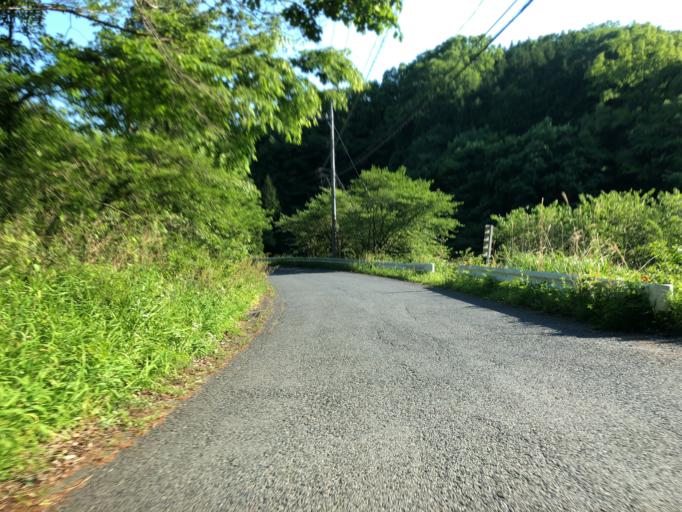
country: JP
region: Ibaraki
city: Kitaibaraki
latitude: 36.8758
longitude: 140.6534
